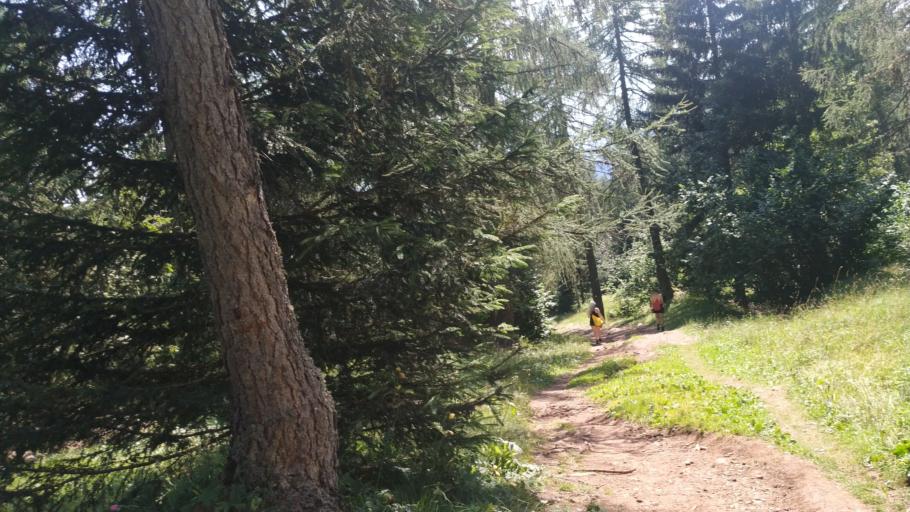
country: IT
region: Trentino-Alto Adige
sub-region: Bolzano
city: San Felice
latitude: 46.4872
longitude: 11.1550
